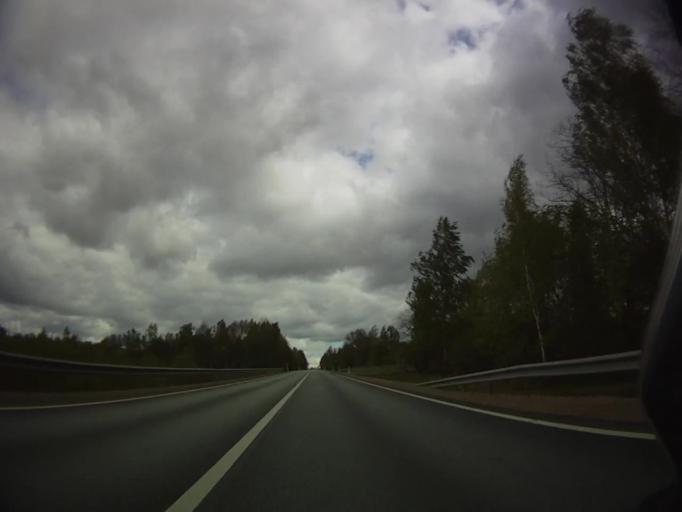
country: LV
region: Sigulda
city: Sigulda
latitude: 57.2291
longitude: 24.8076
